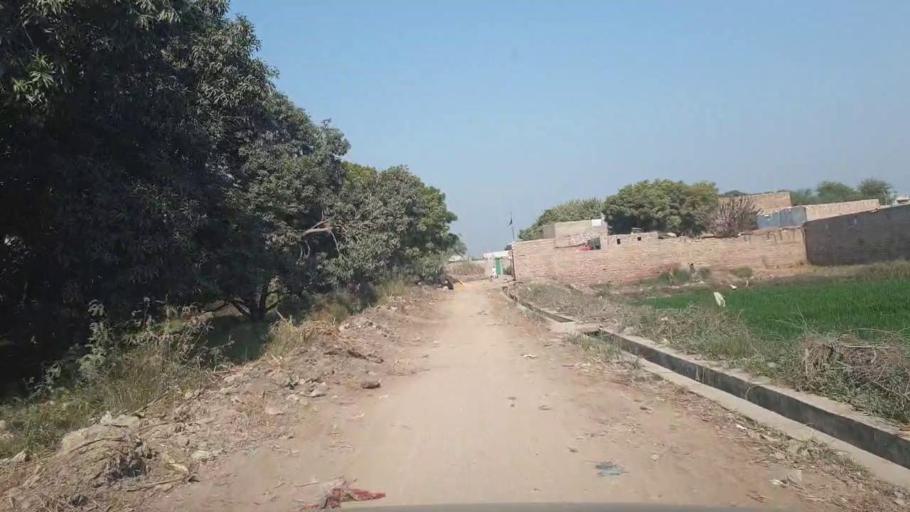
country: PK
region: Sindh
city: Tando Allahyar
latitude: 25.4747
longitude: 68.7834
